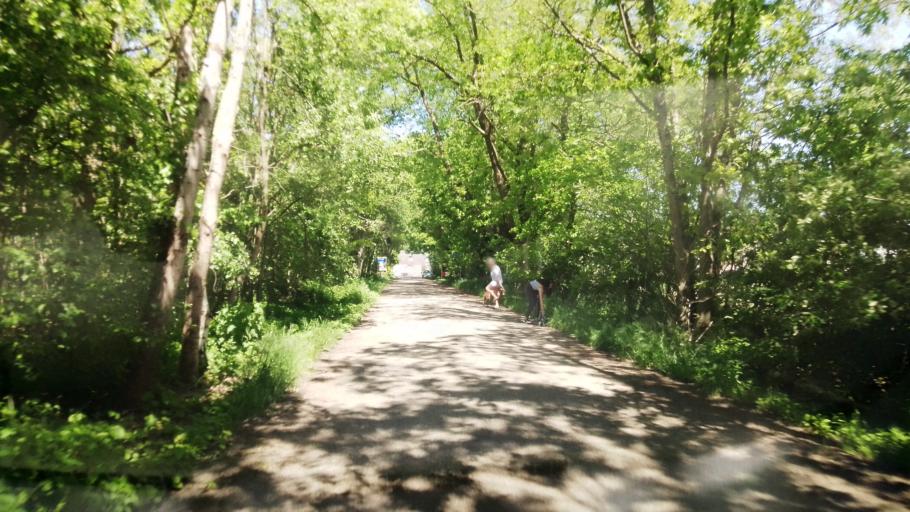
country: NL
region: Limburg
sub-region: Gemeente Venlo
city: Tegelen
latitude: 51.3280
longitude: 6.1552
